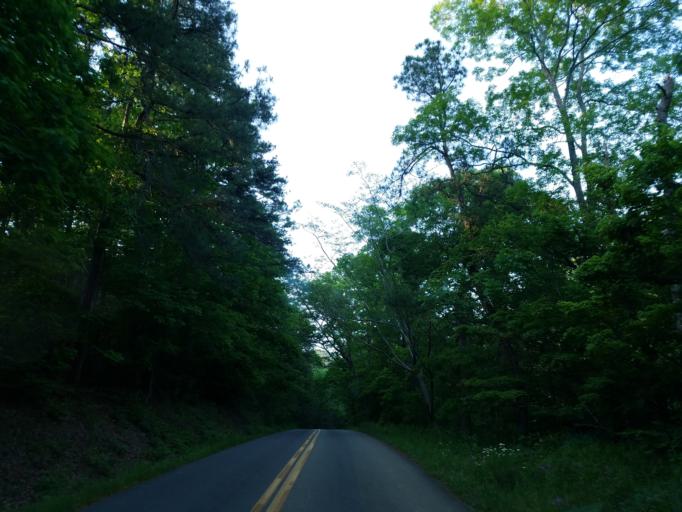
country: US
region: Georgia
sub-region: Gordon County
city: Calhoun
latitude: 34.5731
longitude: -85.0998
